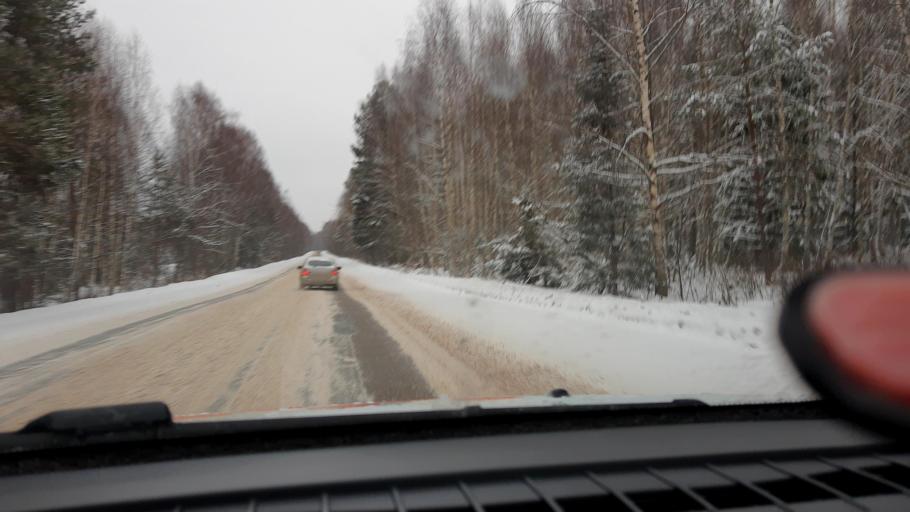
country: RU
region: Nizjnij Novgorod
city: Pamyat' Parizhskoy Kommuny
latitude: 56.2588
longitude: 44.4558
